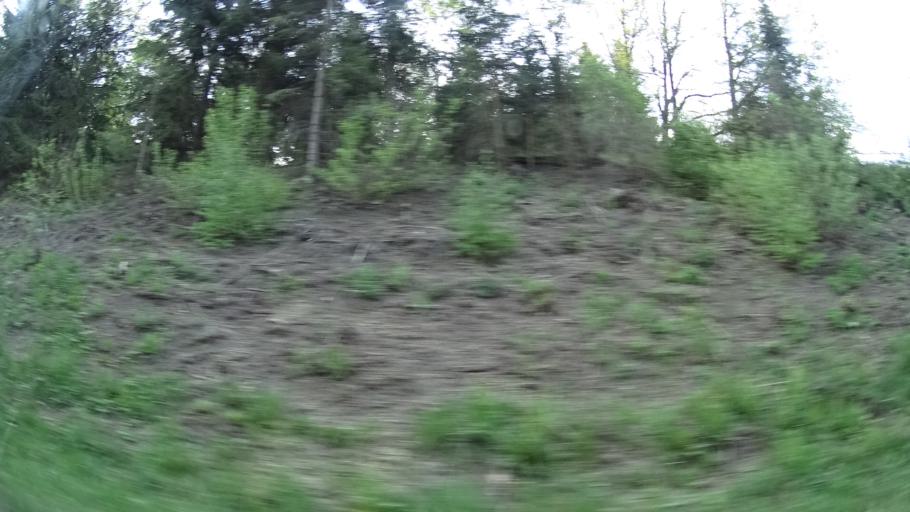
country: DE
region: Baden-Wuerttemberg
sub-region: Freiburg Region
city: Dietingen
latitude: 48.2191
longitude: 8.6581
